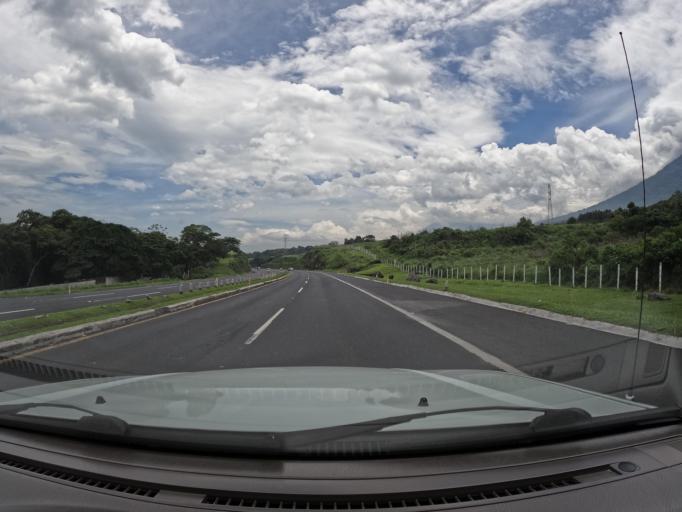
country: GT
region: Escuintla
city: Palin
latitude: 14.3996
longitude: -90.7192
